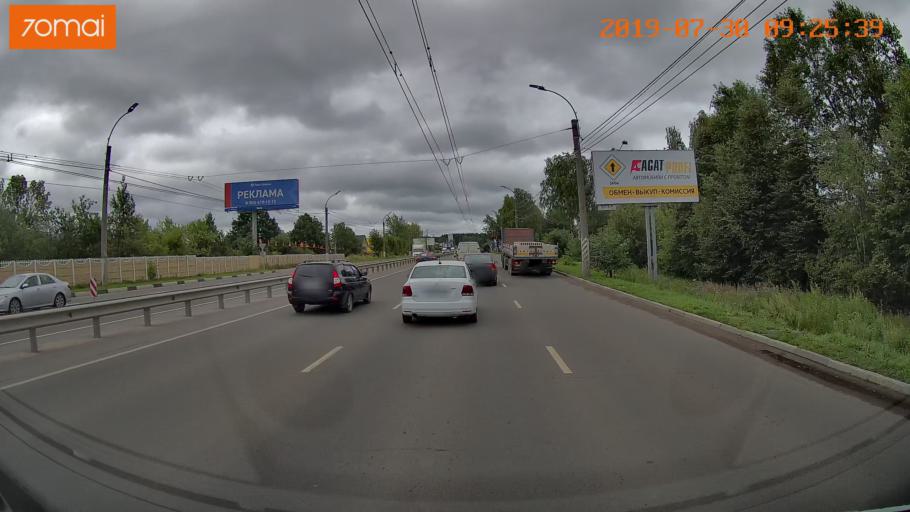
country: RU
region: Ivanovo
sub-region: Gorod Ivanovo
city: Ivanovo
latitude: 56.9513
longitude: 40.9749
